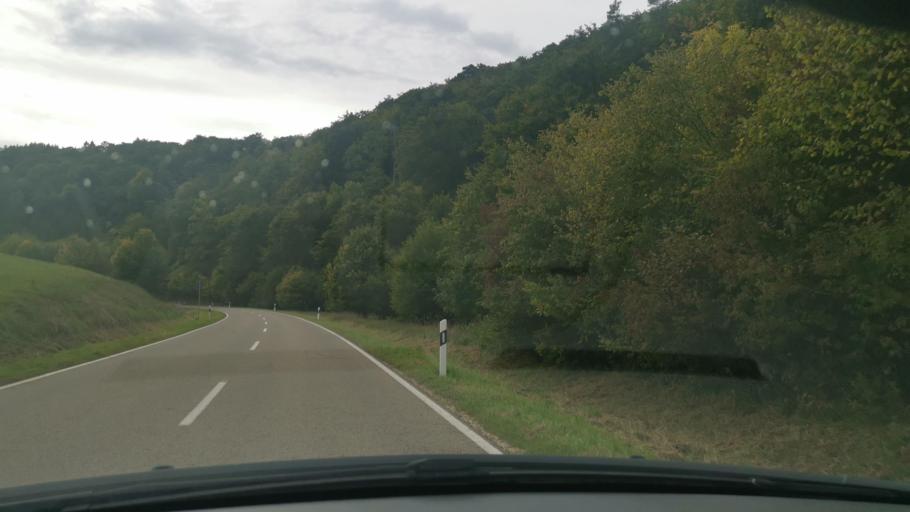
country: DE
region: Baden-Wuerttemberg
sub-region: Tuebingen Region
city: Hayingen
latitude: 48.2992
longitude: 9.5115
